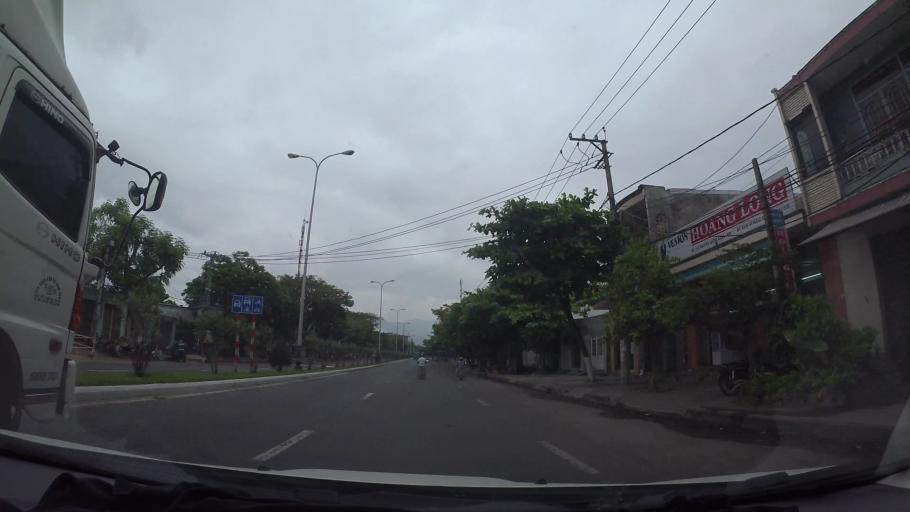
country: VN
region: Da Nang
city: Lien Chieu
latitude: 16.1144
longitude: 108.1273
